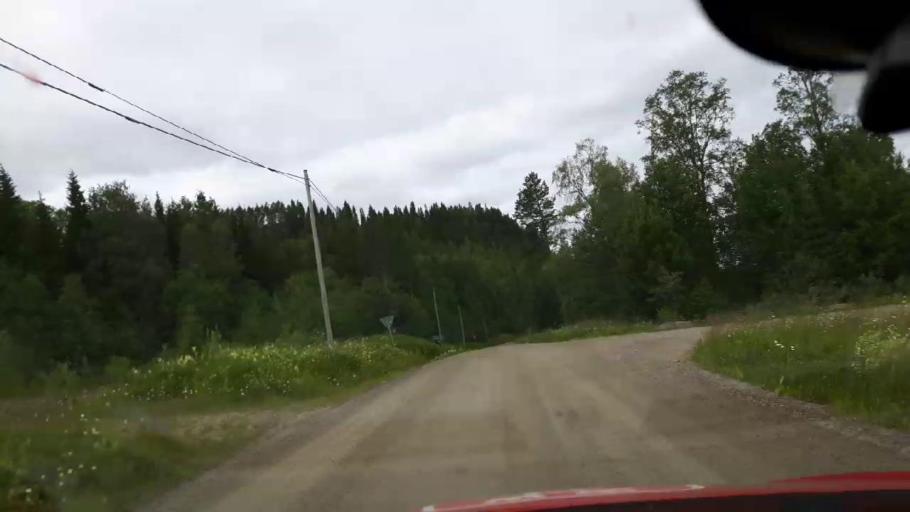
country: SE
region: Jaemtland
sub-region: OEstersunds Kommun
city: Brunflo
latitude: 62.9011
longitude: 15.1150
